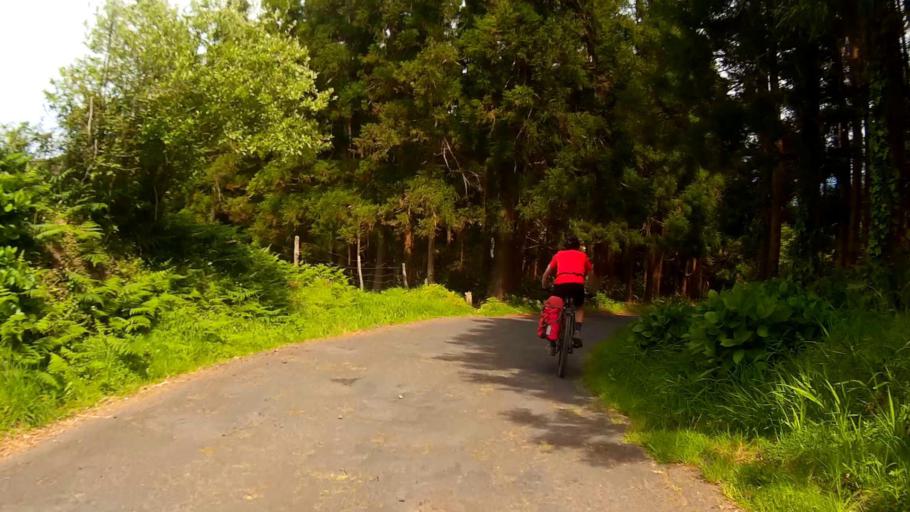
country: PT
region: Azores
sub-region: Horta
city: Horta
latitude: 38.5514
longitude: -28.6674
